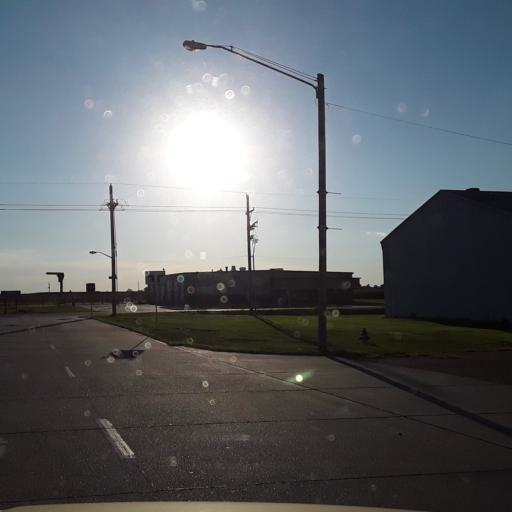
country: US
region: Nebraska
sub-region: Hall County
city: Grand Island
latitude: 40.9707
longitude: -98.3197
